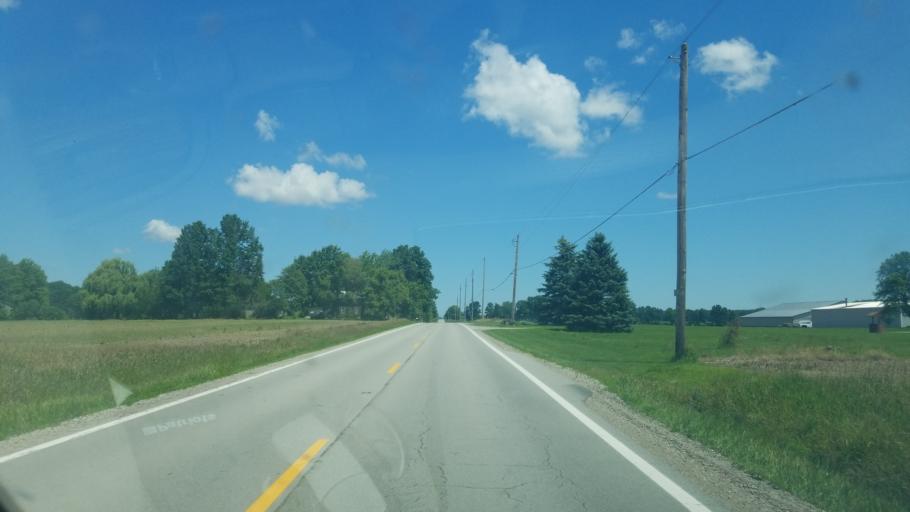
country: US
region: Ohio
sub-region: Huron County
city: New London
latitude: 41.1430
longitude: -82.4098
